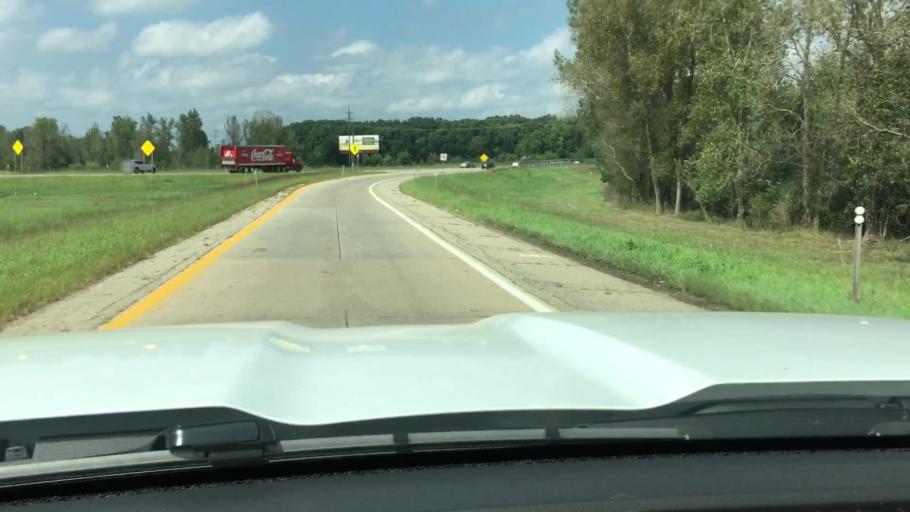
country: US
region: Michigan
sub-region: Allegan County
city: Plainwell
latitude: 42.4508
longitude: -85.6544
